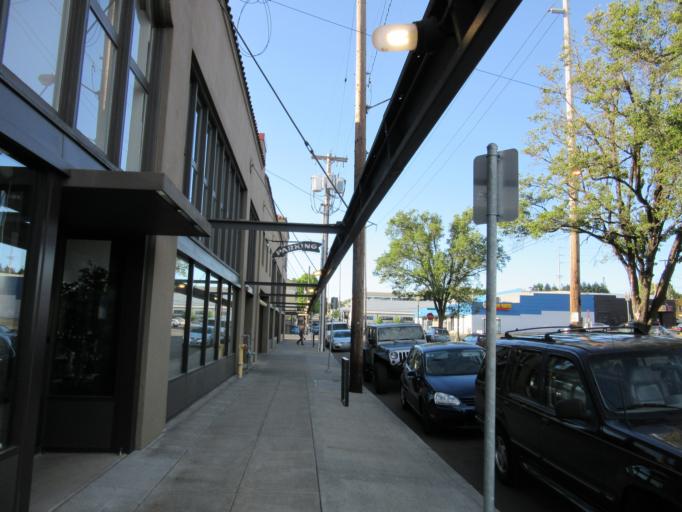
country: US
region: Oregon
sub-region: Multnomah County
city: Portland
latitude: 45.5166
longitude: -122.6568
